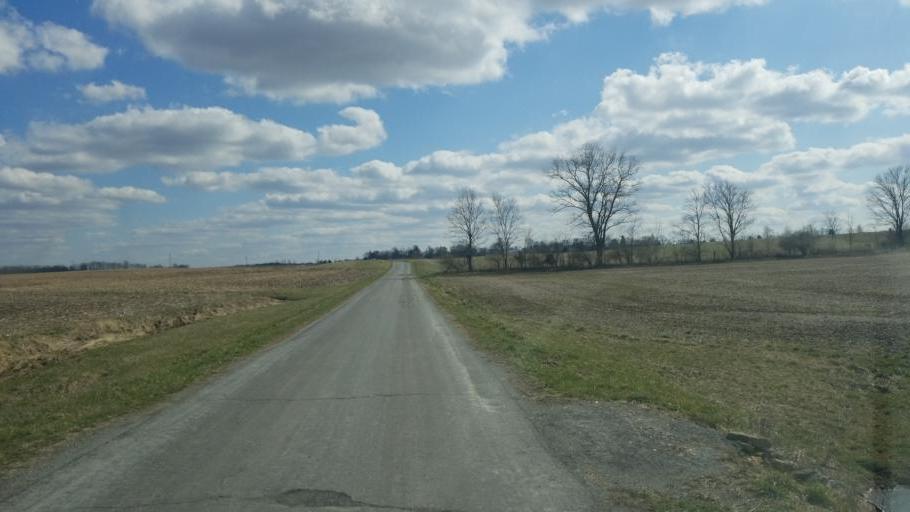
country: US
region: Ohio
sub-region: Highland County
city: Greenfield
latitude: 39.2720
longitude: -83.4455
